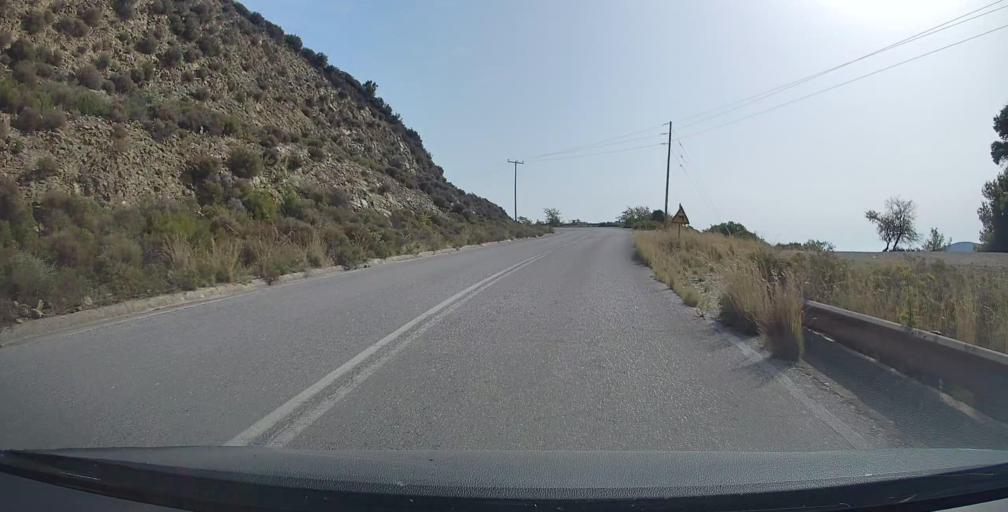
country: GR
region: Central Macedonia
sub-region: Nomos Chalkidikis
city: Sykia
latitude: 39.9685
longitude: 23.9542
